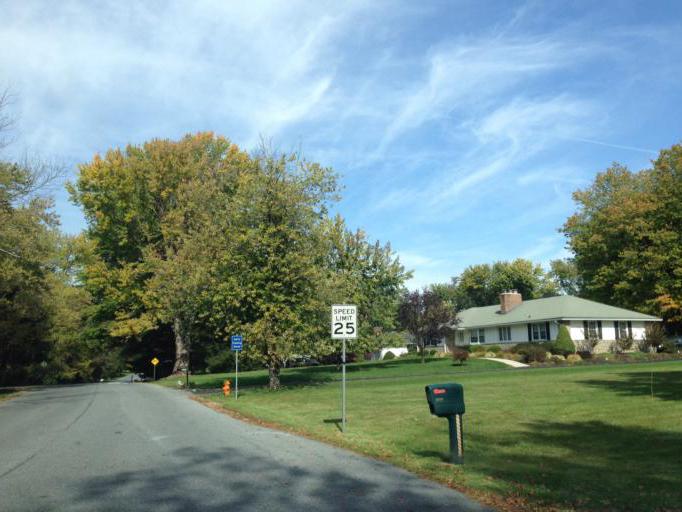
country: US
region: Maryland
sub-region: Howard County
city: Columbia
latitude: 39.2784
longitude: -76.8388
